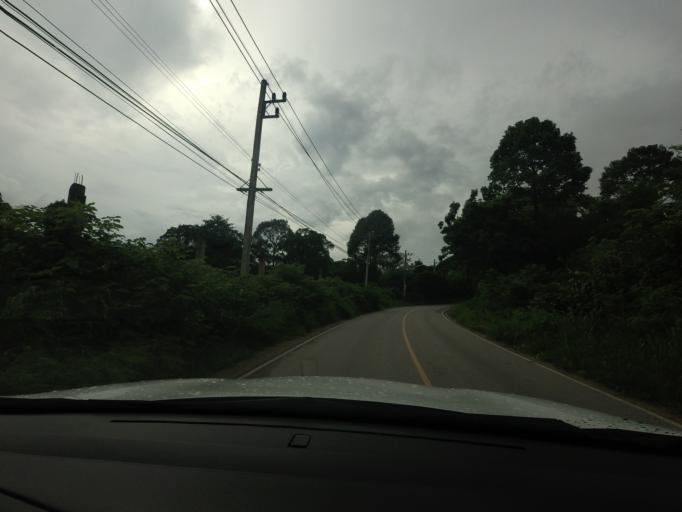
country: TH
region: Nakhon Ratchasima
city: Pak Chong
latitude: 14.6177
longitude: 101.4441
